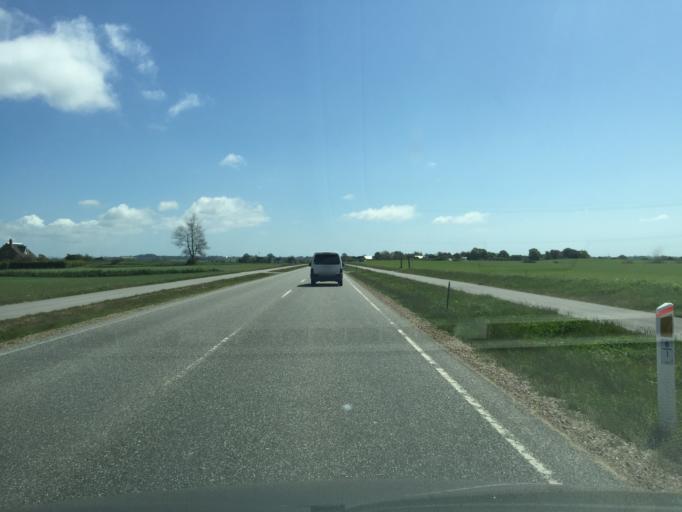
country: DK
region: Zealand
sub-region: Vordingborg Kommune
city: Stege
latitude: 54.9797
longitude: 12.1831
